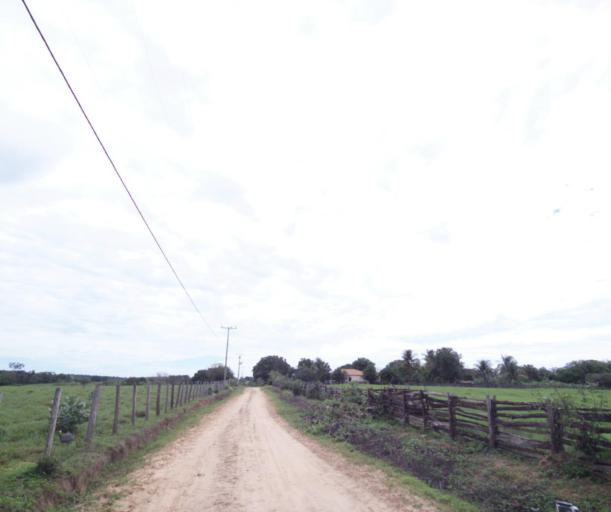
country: BR
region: Bahia
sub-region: Carinhanha
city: Carinhanha
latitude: -14.2504
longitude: -44.3514
